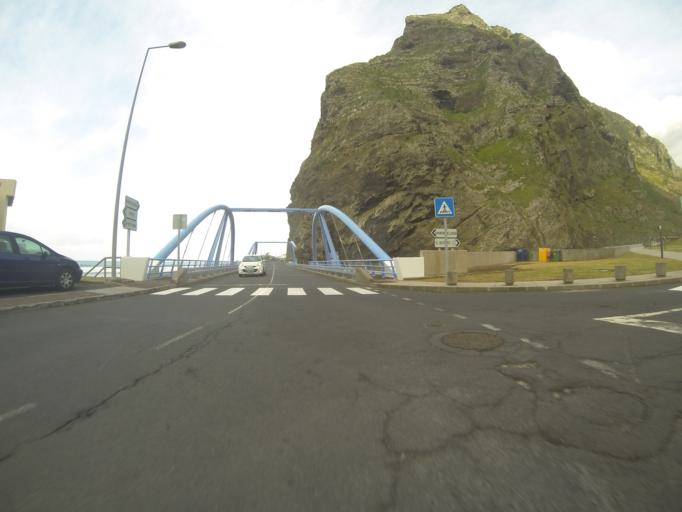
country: PT
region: Madeira
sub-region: Sao Vicente
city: Sao Vicente
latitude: 32.8091
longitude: -17.0474
